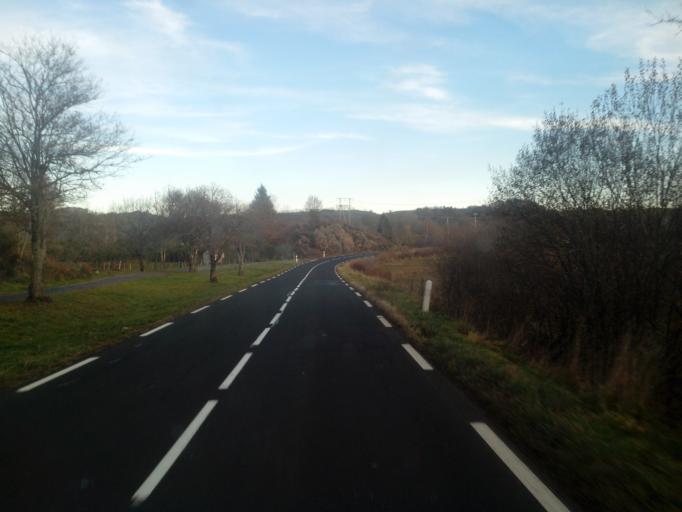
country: FR
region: Auvergne
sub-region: Departement du Cantal
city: Riom-es-Montagnes
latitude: 45.2994
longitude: 2.6131
